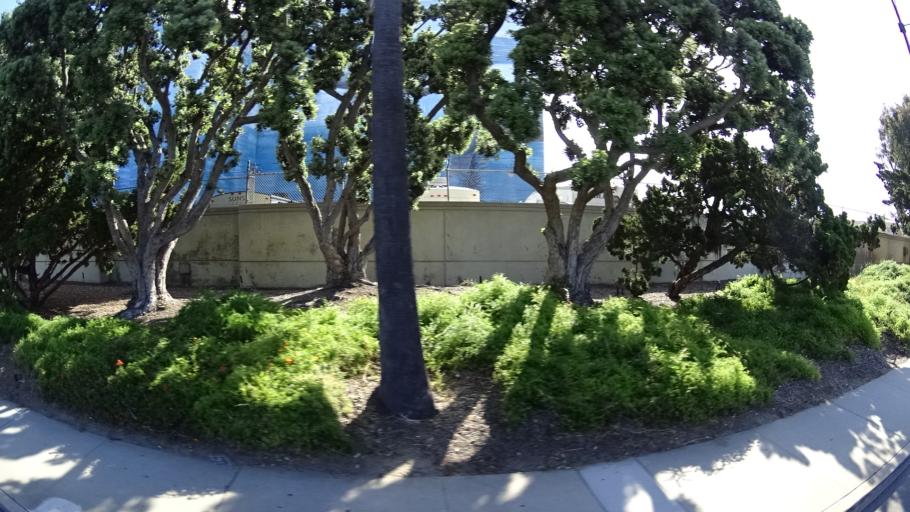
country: US
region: California
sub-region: Los Angeles County
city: Redondo Beach
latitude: 33.8481
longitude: -118.3949
